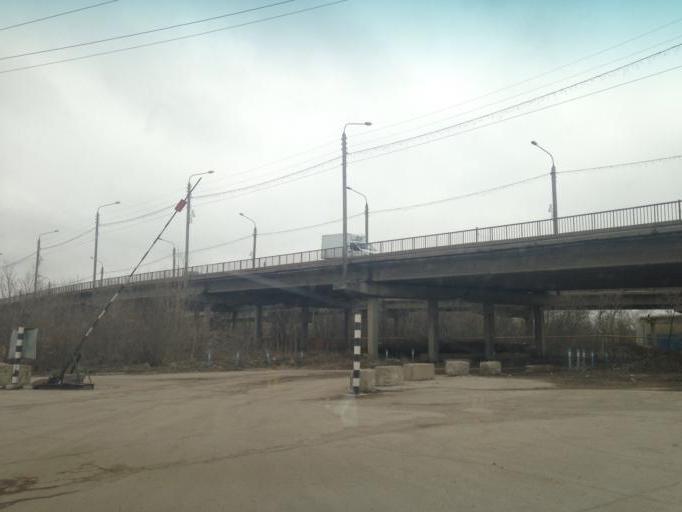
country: RU
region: Ulyanovsk
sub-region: Ulyanovskiy Rayon
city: Ulyanovsk
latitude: 54.3052
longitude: 48.3086
